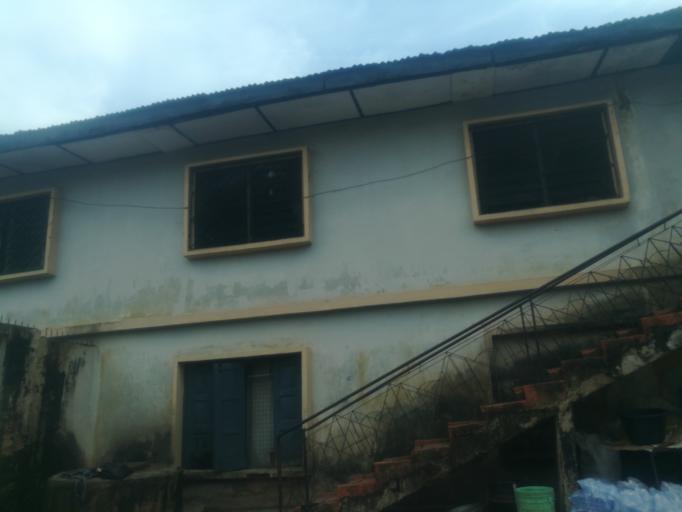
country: NG
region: Oyo
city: Ibadan
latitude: 7.4144
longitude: 3.8964
